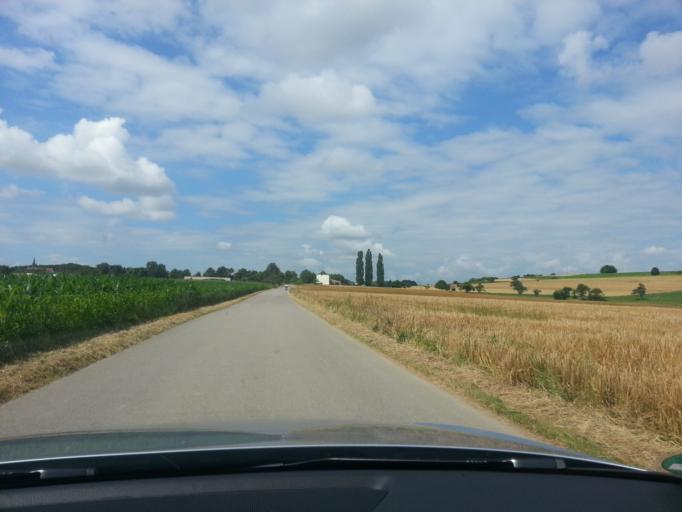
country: DE
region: Rheinland-Pfalz
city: Kirf
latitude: 49.5176
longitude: 6.4880
